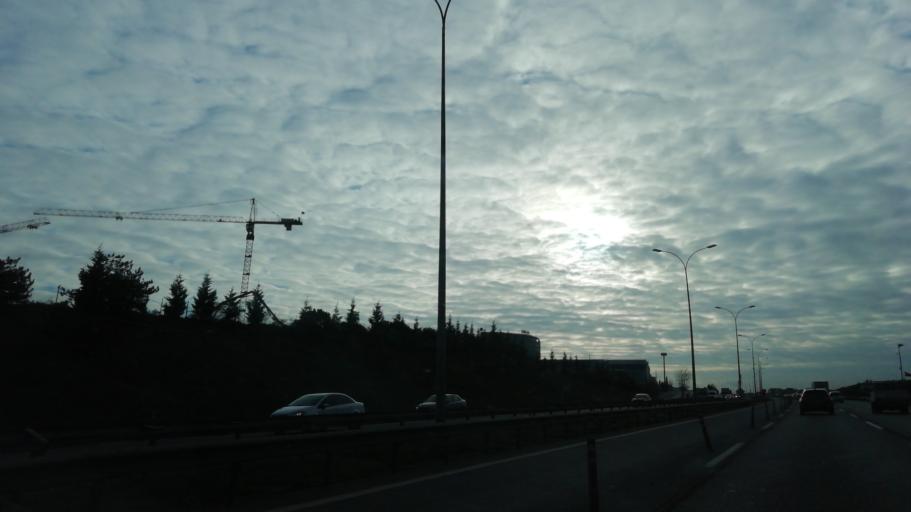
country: TR
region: Kocaeli
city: Balcik
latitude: 40.8876
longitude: 29.3741
